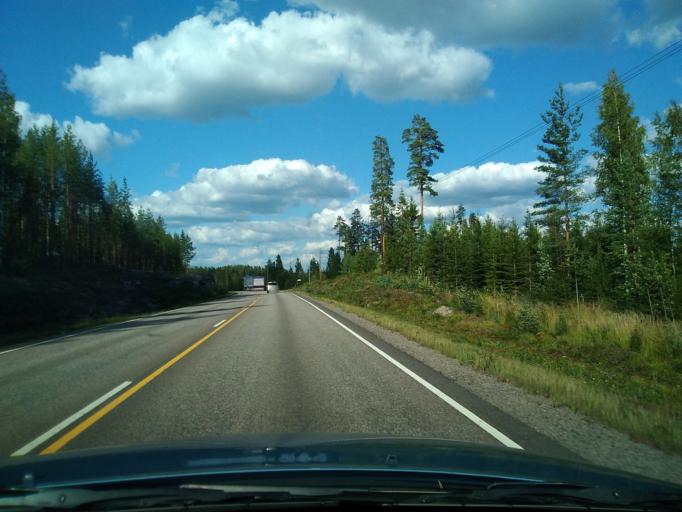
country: FI
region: Pirkanmaa
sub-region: Ylae-Pirkanmaa
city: Maenttae
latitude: 62.1140
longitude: 24.7425
